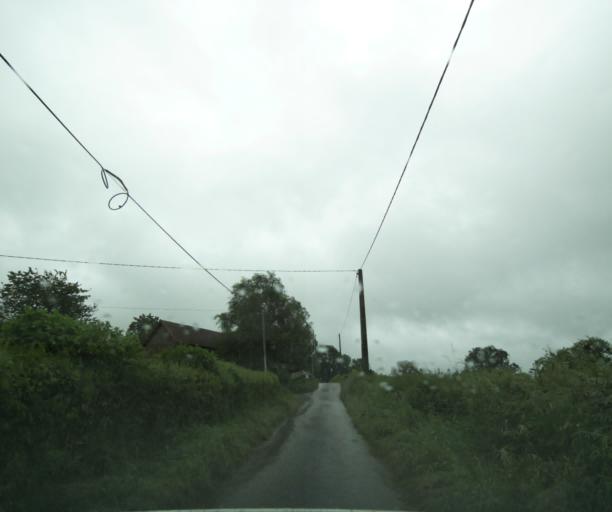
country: FR
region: Bourgogne
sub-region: Departement de Saone-et-Loire
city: Charolles
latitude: 46.4977
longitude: 4.3976
